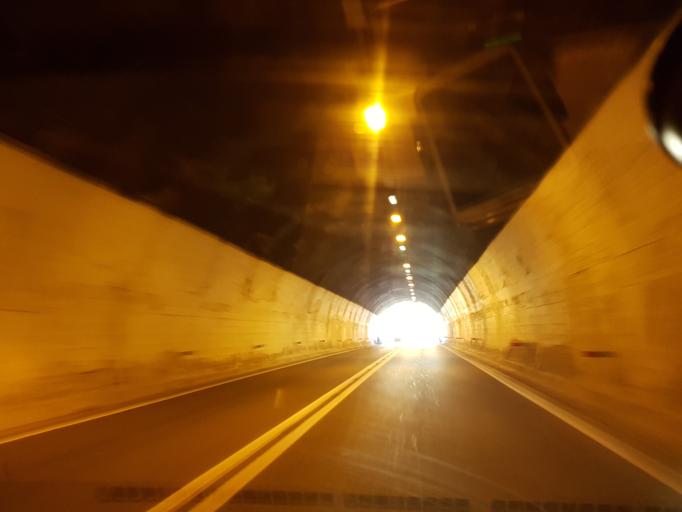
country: IT
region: Liguria
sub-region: Provincia di Genova
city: Genoa
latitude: 44.4351
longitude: 8.9418
